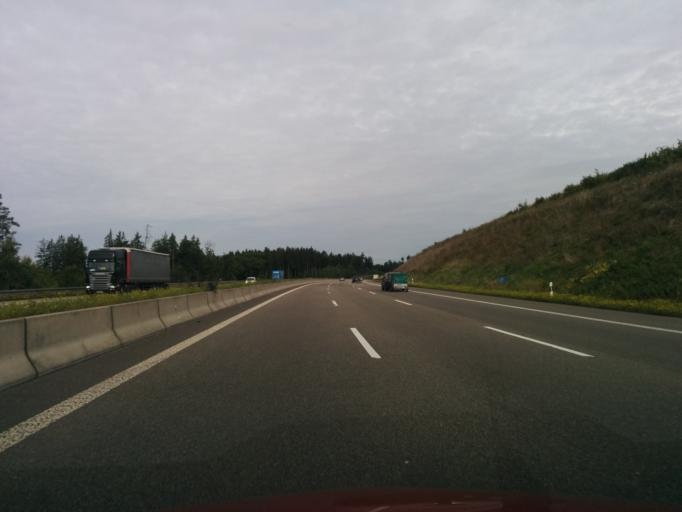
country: DE
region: Baden-Wuerttemberg
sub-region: Karlsruhe Region
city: Tiefenbronn
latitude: 48.8488
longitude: 8.8049
